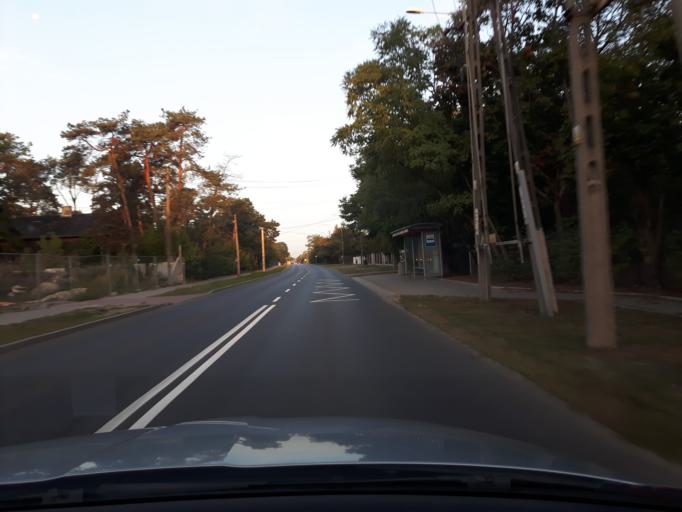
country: PL
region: Masovian Voivodeship
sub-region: Warszawa
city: Wawer
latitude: 52.1842
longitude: 21.1835
